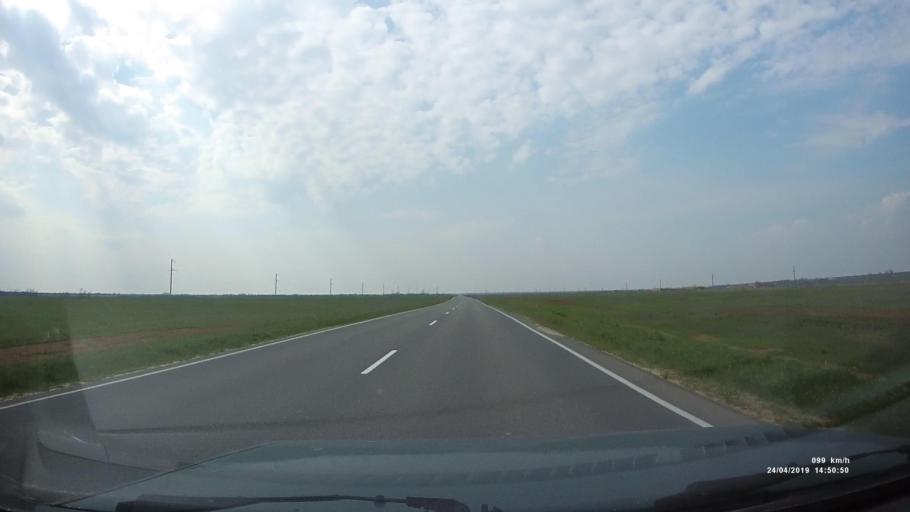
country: RU
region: Rostov
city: Remontnoye
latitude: 46.5203
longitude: 43.7119
